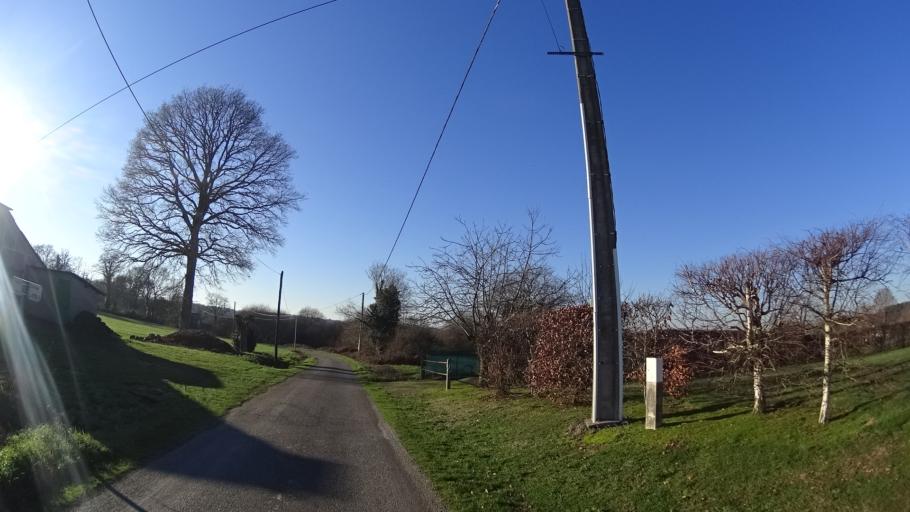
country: FR
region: Brittany
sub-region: Departement du Morbihan
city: Allaire
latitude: 47.6563
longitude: -2.1766
